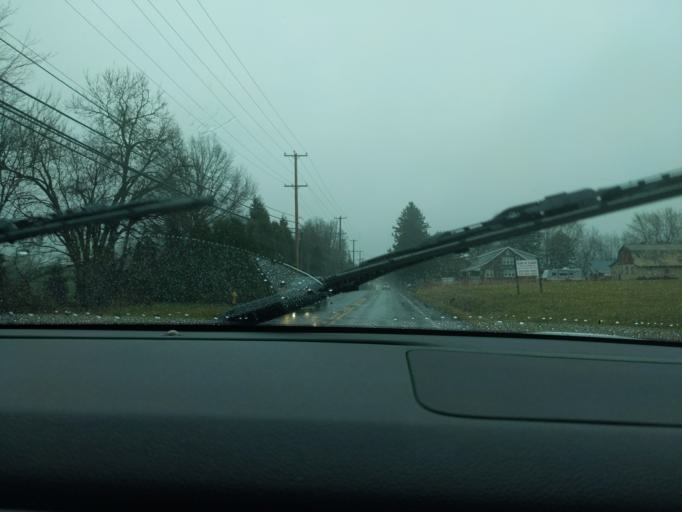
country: US
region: Pennsylvania
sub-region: Bucks County
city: Dublin
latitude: 40.3667
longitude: -75.1949
